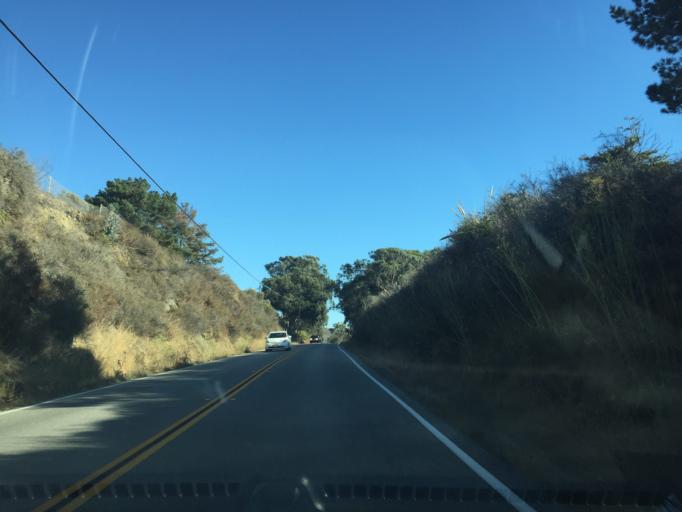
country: US
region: California
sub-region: Monterey County
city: King City
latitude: 35.8807
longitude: -121.4510
